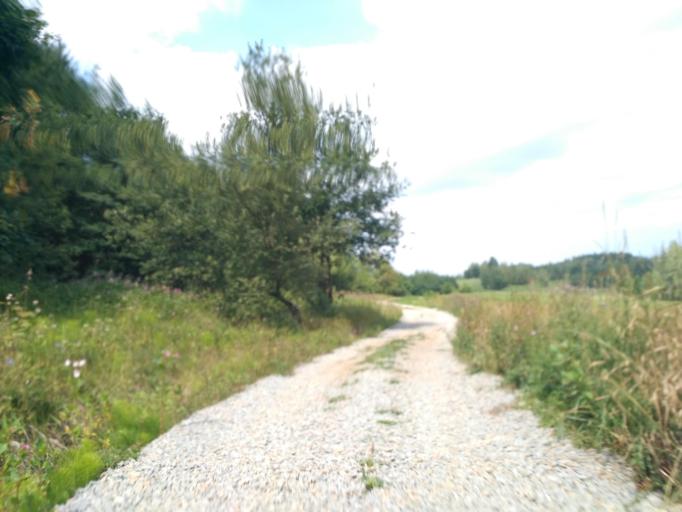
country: PL
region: Subcarpathian Voivodeship
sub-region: Powiat krosnienski
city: Iwonicz-Zdroj
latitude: 49.5729
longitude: 21.8100
